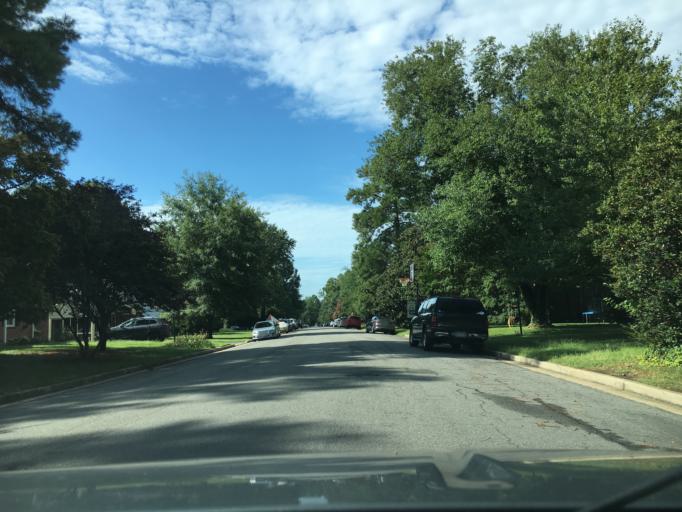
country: US
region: Virginia
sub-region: Henrico County
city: Tuckahoe
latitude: 37.5919
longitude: -77.5341
